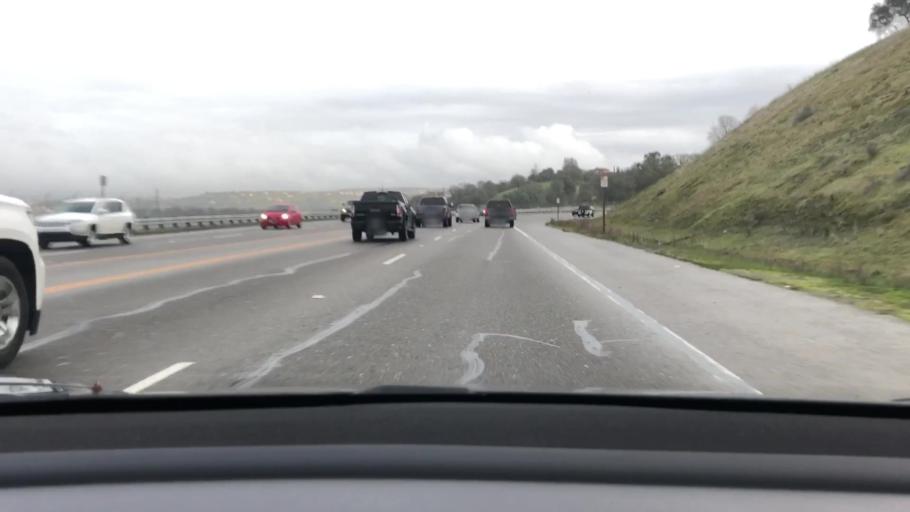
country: US
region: California
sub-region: Sacramento County
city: Folsom
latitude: 38.7001
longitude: -121.1455
